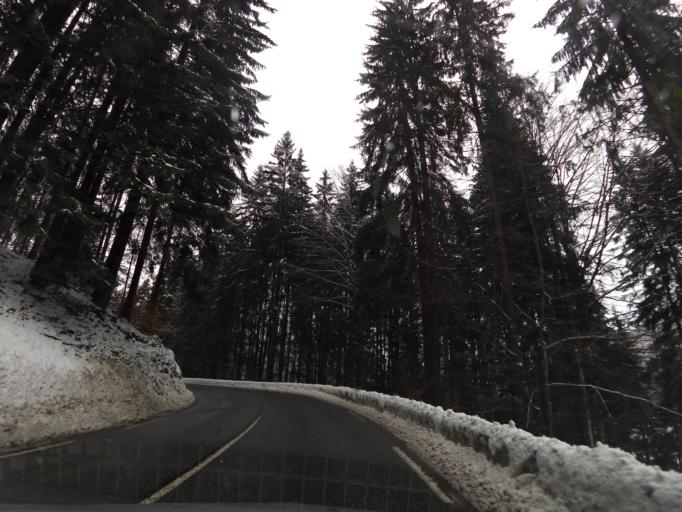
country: FR
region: Rhone-Alpes
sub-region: Departement de la Haute-Savoie
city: Morzine
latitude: 46.1908
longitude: 6.6876
